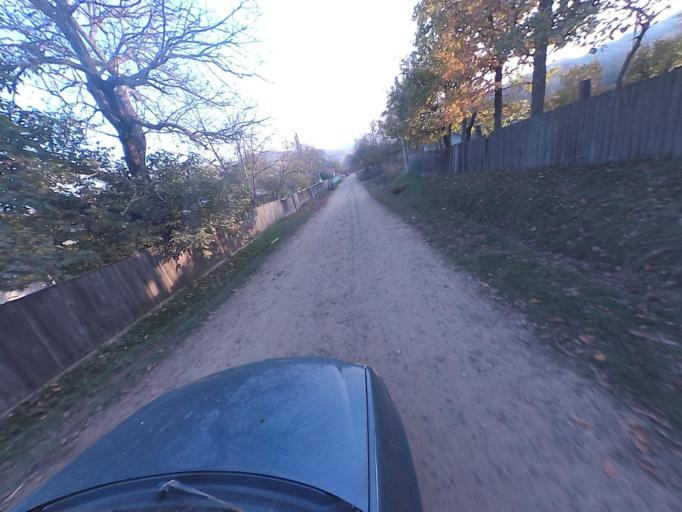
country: RO
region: Vaslui
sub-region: Comuna Bacesti
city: Bacesti
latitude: 46.8014
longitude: 27.2243
